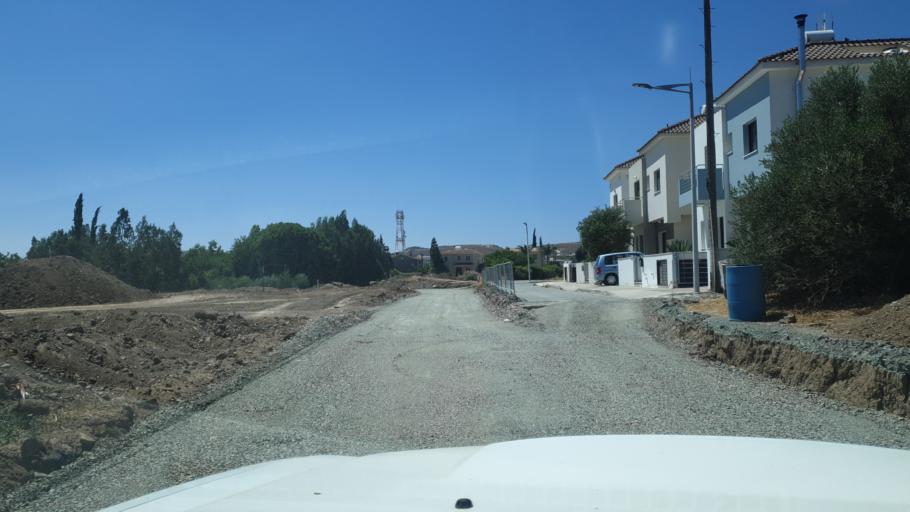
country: CY
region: Lefkosia
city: Dali
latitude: 35.0214
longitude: 33.4088
